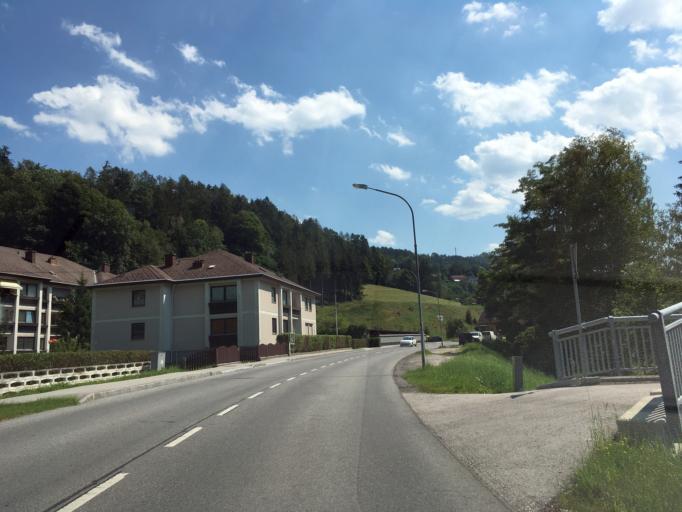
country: AT
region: Lower Austria
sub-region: Politischer Bezirk Neunkirchen
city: Edlitz
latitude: 47.5954
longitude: 16.1440
